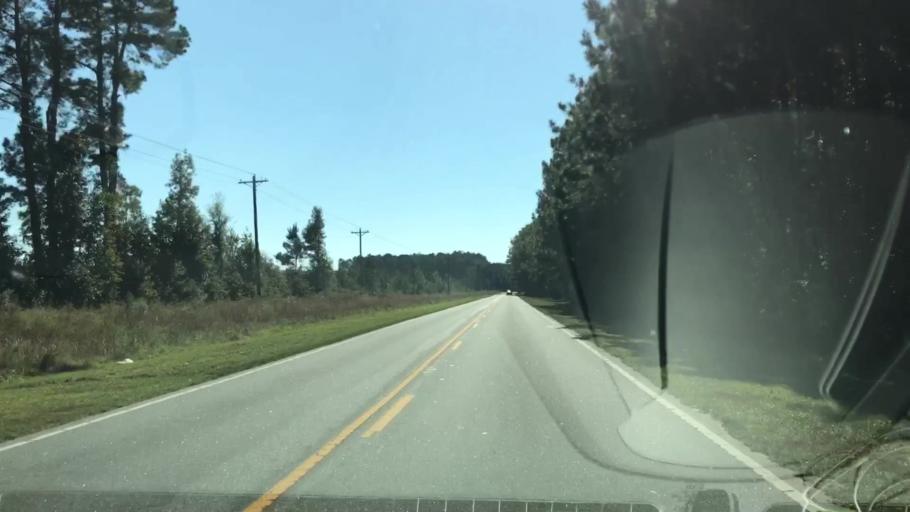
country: US
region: South Carolina
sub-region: Jasper County
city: Ridgeland
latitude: 32.4452
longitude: -80.8962
